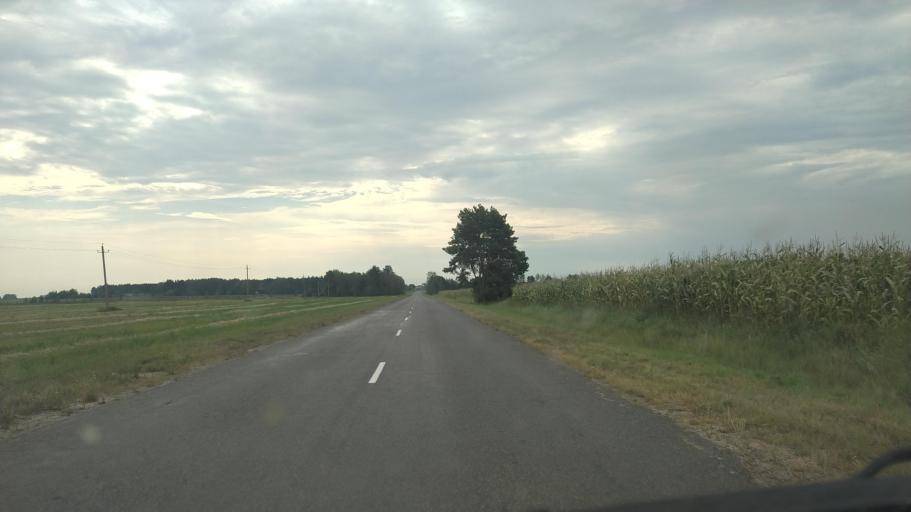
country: BY
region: Brest
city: Byaroza
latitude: 52.5642
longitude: 24.9030
